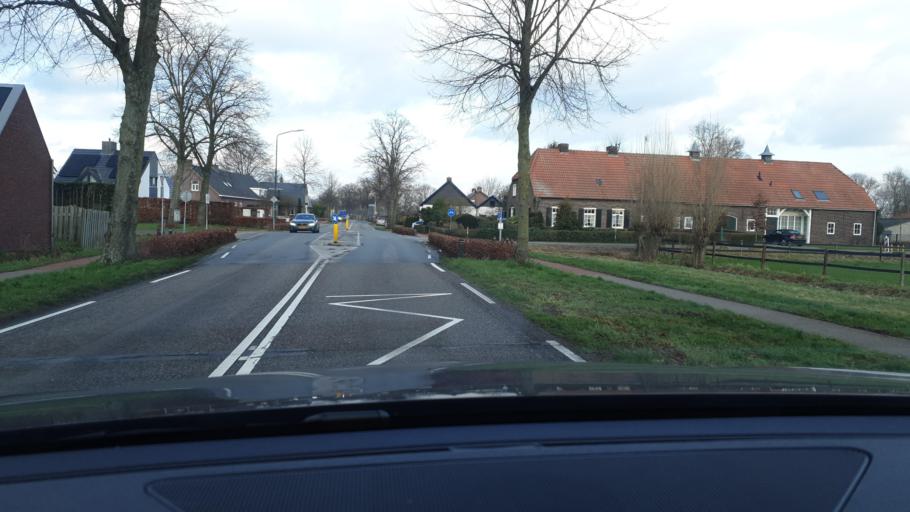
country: NL
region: North Brabant
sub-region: Gemeente Valkenswaard
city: Valkenswaard
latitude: 51.3363
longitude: 5.4097
